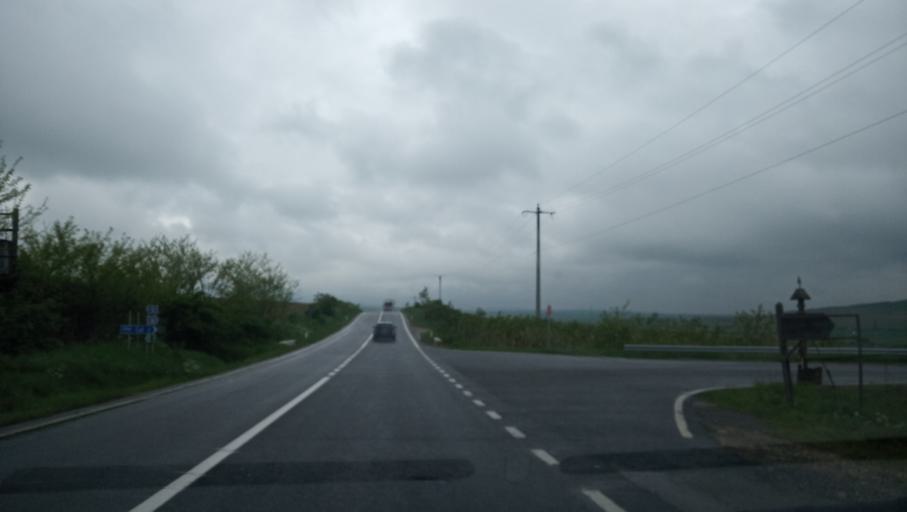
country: RO
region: Alba
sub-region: Comuna Cut
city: Cut
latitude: 45.9203
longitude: 23.6591
